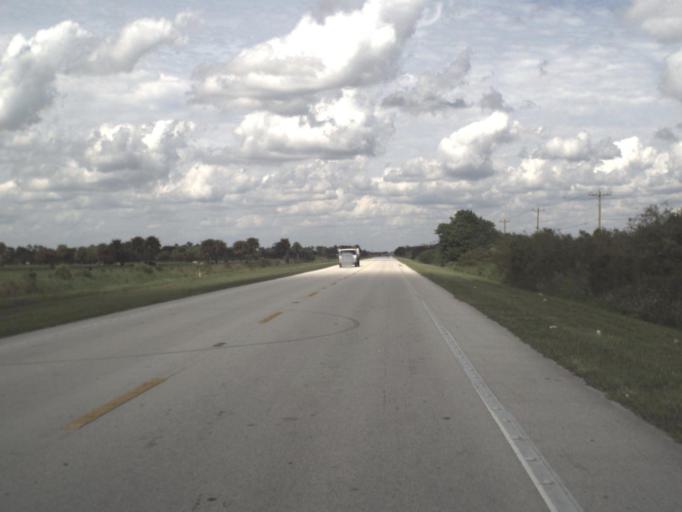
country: US
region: Florida
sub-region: Collier County
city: Immokalee
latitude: 26.4952
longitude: -81.4348
